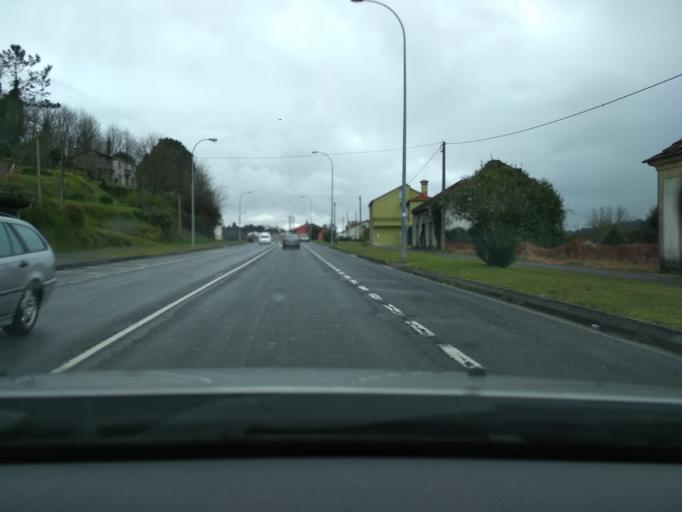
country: ES
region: Galicia
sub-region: Provincia da Coruna
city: Padron
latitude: 42.7640
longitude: -8.6519
